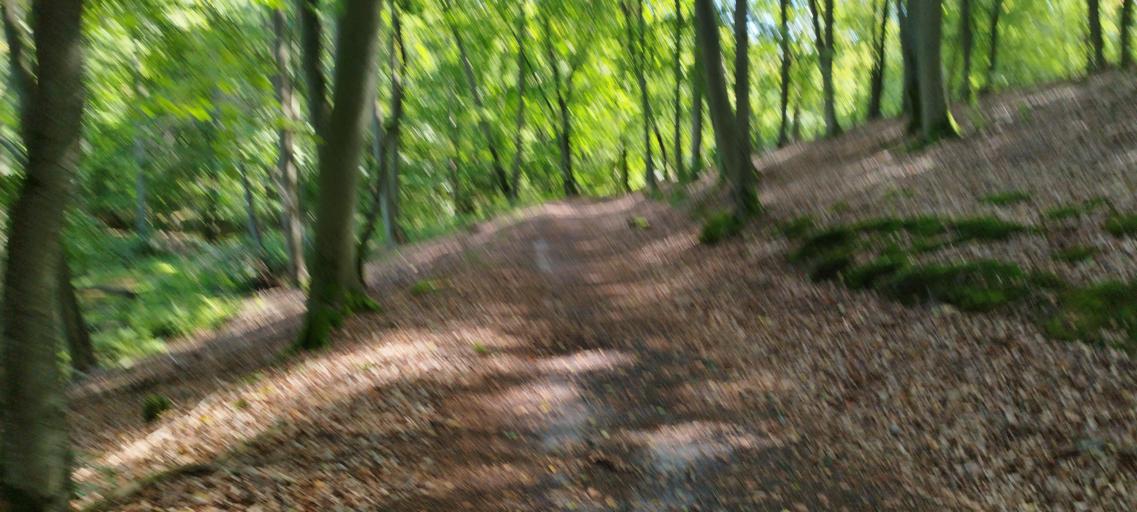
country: DE
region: Brandenburg
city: Mixdorf
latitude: 52.0948
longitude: 14.4847
